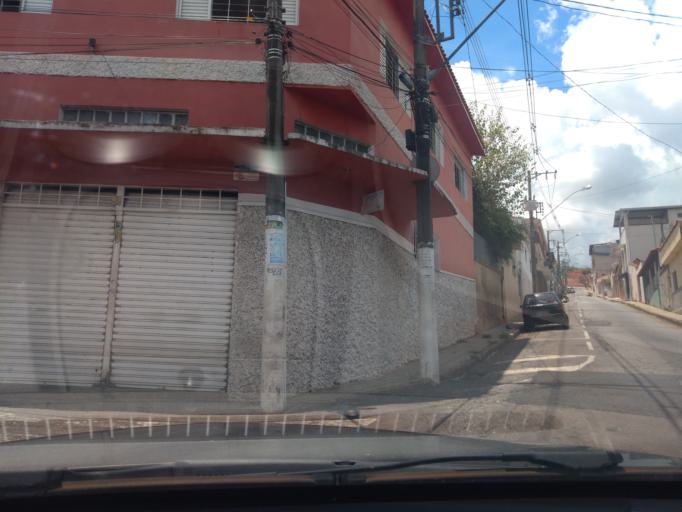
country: BR
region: Minas Gerais
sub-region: Tres Coracoes
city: Tres Coracoes
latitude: -21.6908
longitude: -45.2558
